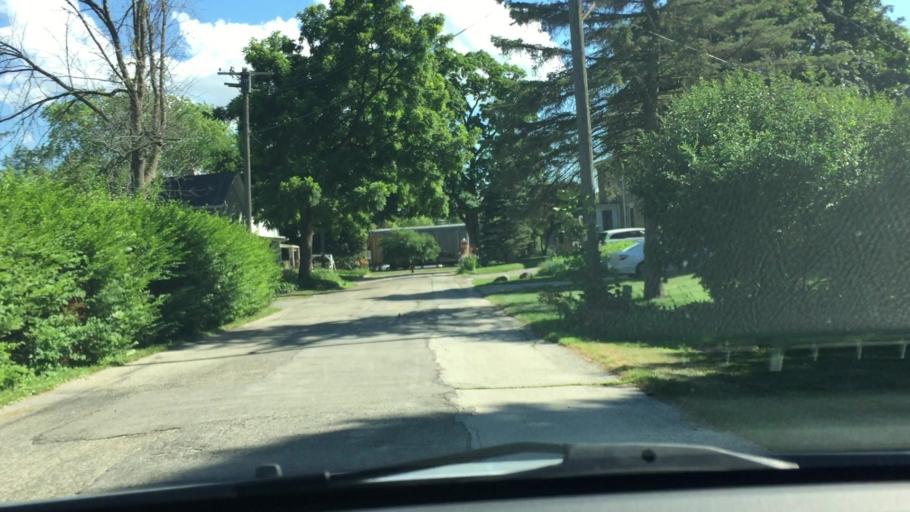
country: US
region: Wisconsin
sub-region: Waukesha County
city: Pewaukee
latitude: 43.0844
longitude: -88.2572
